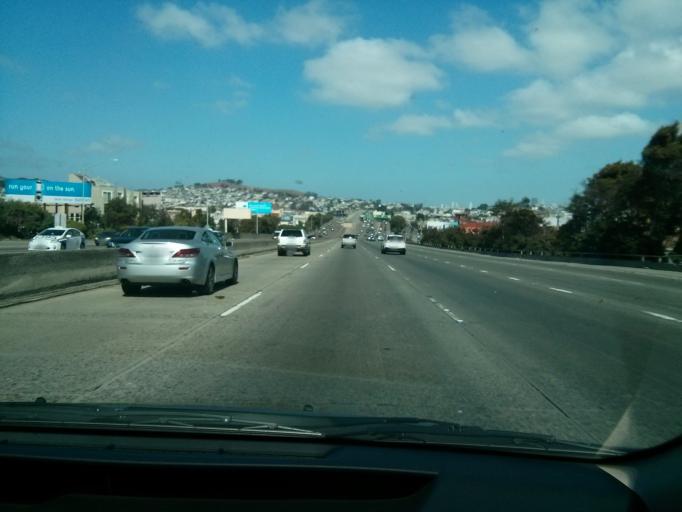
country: US
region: California
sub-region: San Mateo County
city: Brisbane
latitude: 37.7221
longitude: -122.4005
